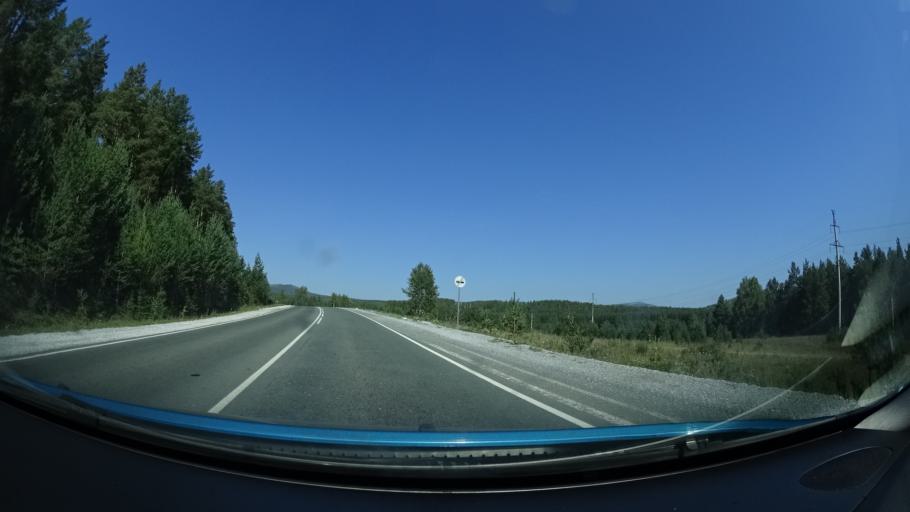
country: RU
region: Bashkortostan
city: Abzakovo
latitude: 53.8531
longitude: 58.5805
